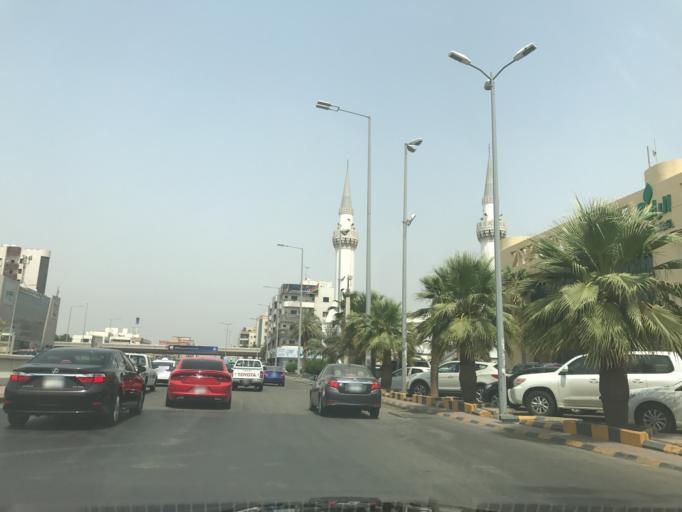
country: SA
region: Makkah
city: Jeddah
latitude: 21.5801
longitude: 39.1630
